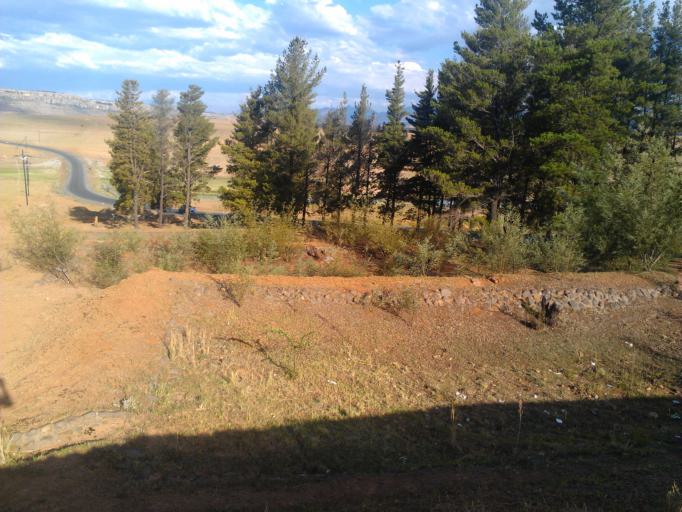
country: LS
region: Berea
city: Teyateyaneng
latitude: -29.1348
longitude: 27.7688
